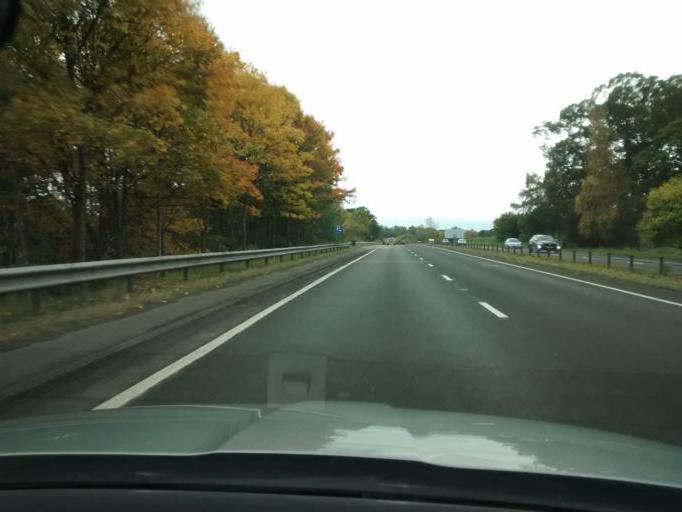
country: GB
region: Scotland
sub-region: Perth and Kinross
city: Luncarty
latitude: 56.4417
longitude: -3.4720
